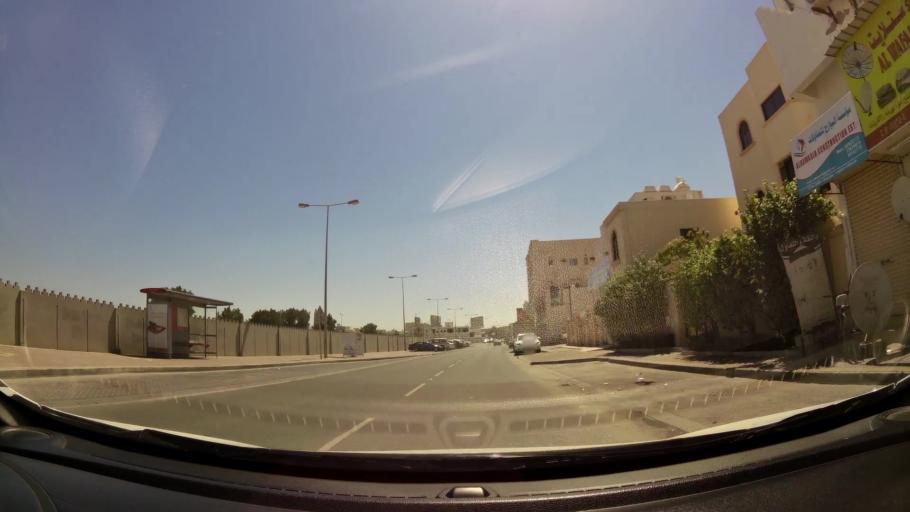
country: BH
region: Muharraq
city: Al Muharraq
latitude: 26.2644
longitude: 50.6094
